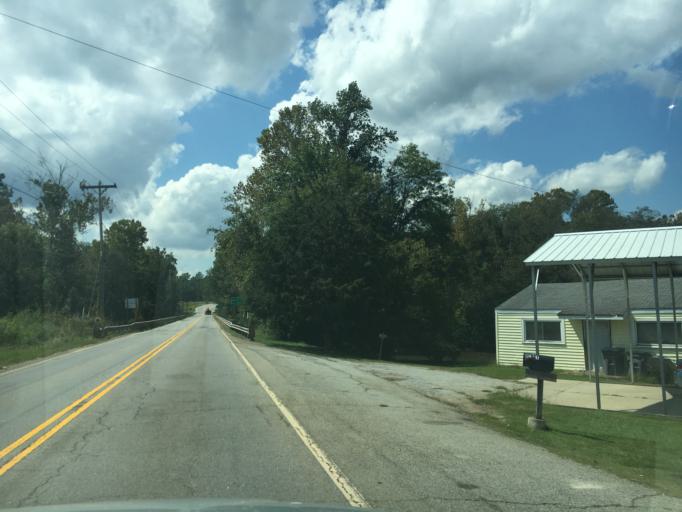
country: US
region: South Carolina
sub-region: Greenville County
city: Berea
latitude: 34.8897
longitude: -82.4953
